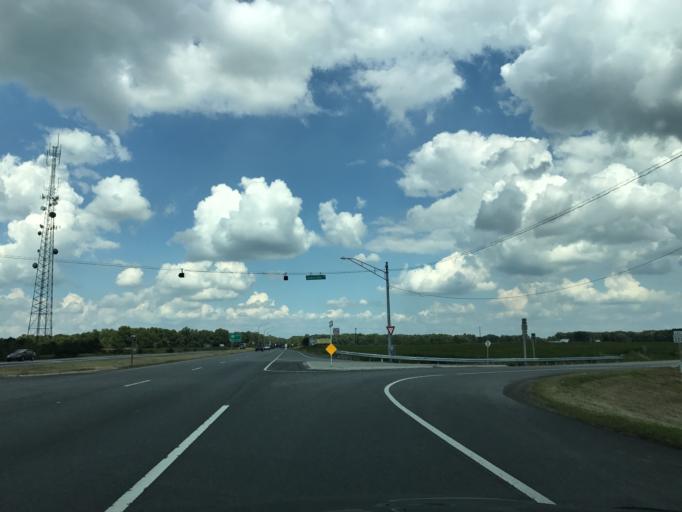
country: US
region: Maryland
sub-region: Queen Anne's County
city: Kingstown
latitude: 39.1730
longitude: -75.9176
